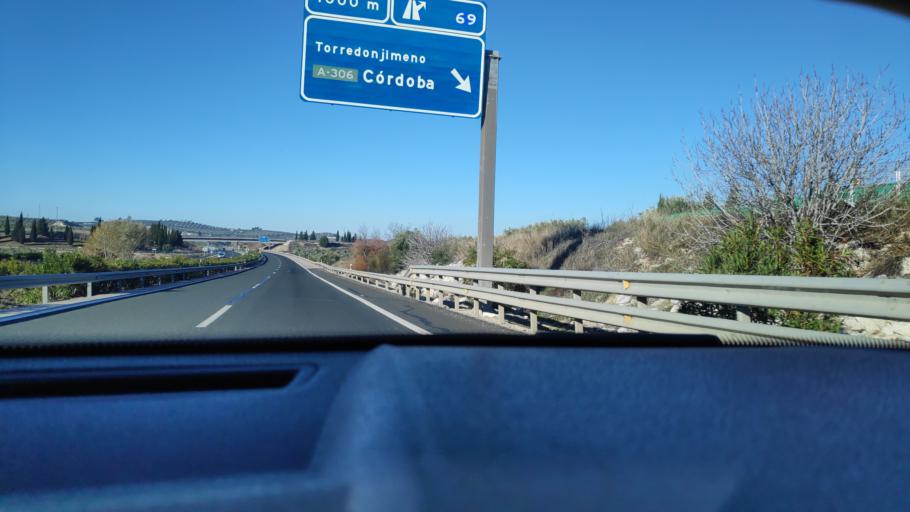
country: ES
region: Andalusia
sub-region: Provincia de Jaen
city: Torredonjimeno
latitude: 37.7532
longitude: -3.9412
